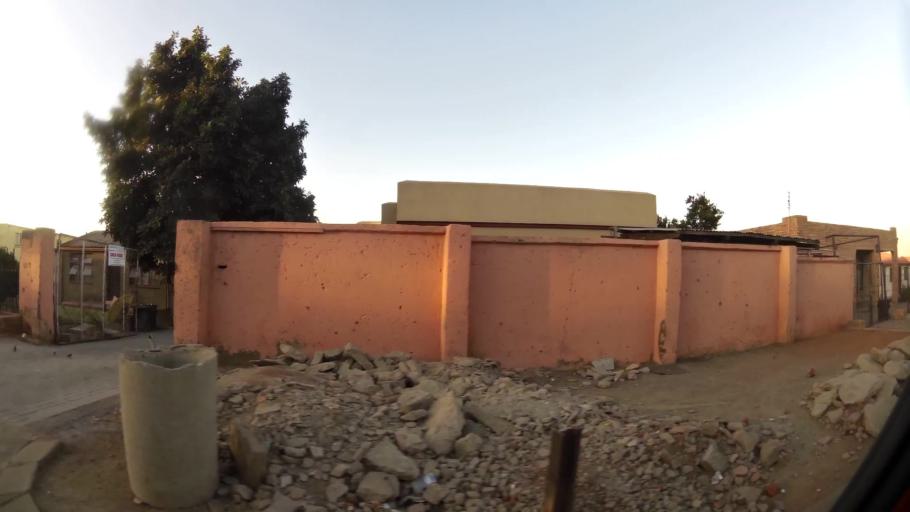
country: ZA
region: North-West
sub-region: Bojanala Platinum District Municipality
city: Rustenburg
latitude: -25.6446
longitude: 27.2142
